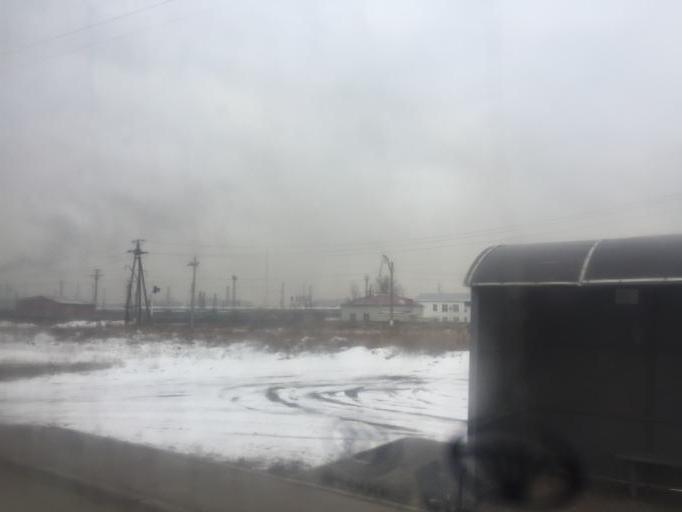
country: KZ
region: Astana Qalasy
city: Astana
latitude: 51.1985
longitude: 71.4119
